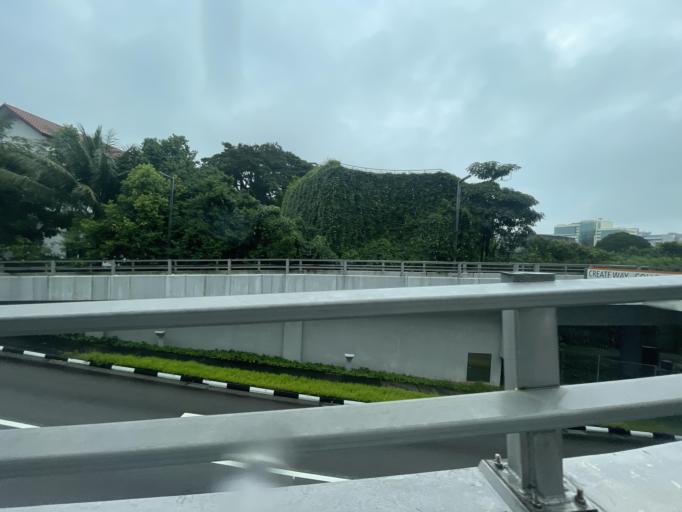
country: SG
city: Singapore
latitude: 1.3036
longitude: 103.7747
